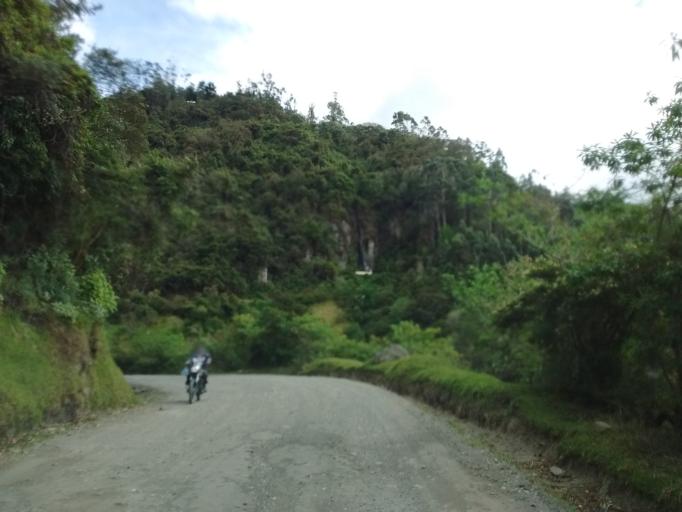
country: CO
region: Cauca
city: Totoro
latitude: 2.3801
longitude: -76.4492
